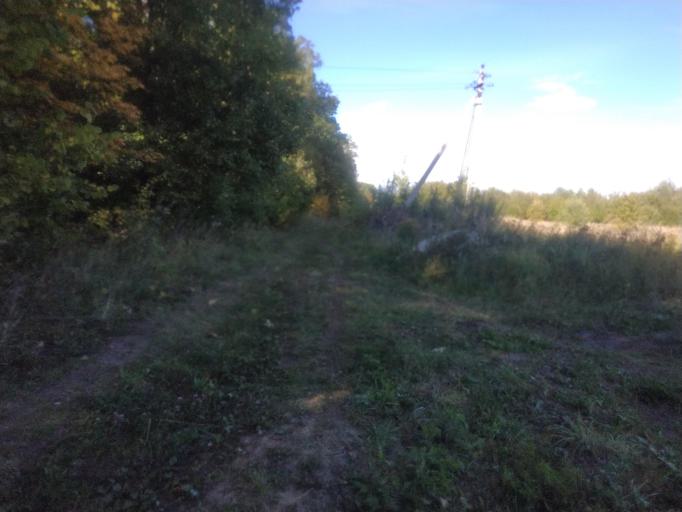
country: RU
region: Chuvashia
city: Novyye Lapsary
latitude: 56.1430
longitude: 47.1382
